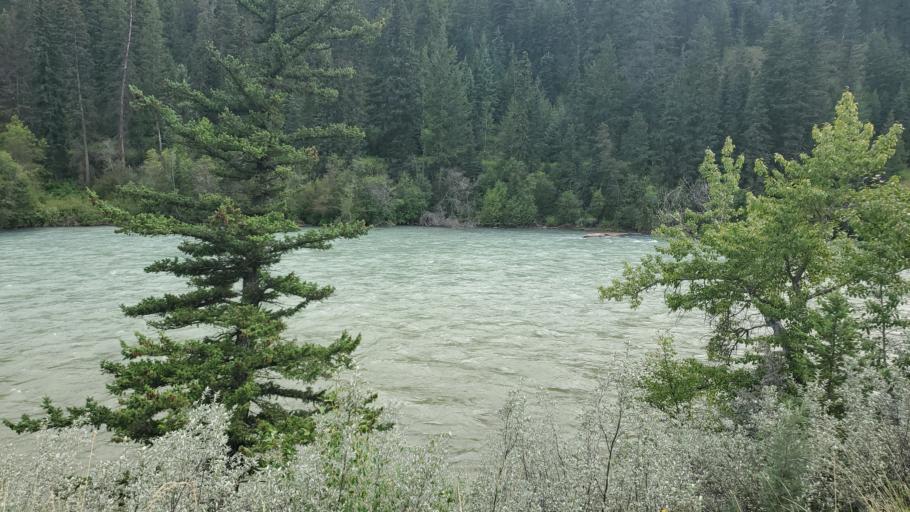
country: CA
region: British Columbia
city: Hanceville
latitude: 52.0868
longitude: -123.3949
